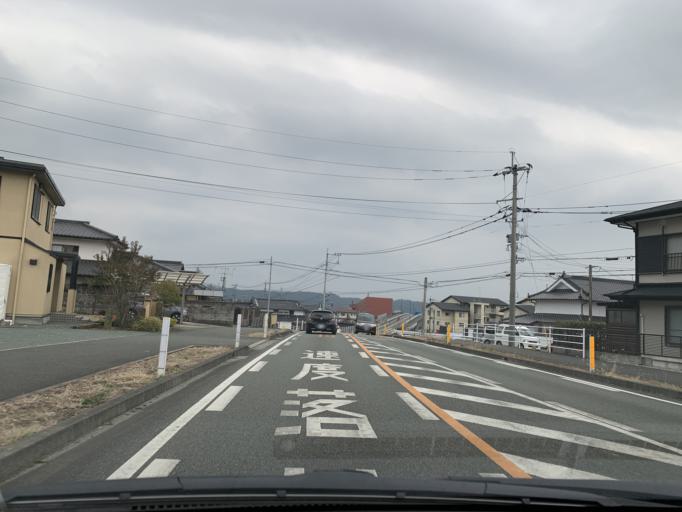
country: JP
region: Kumamoto
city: Ozu
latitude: 32.8794
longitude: 130.8768
